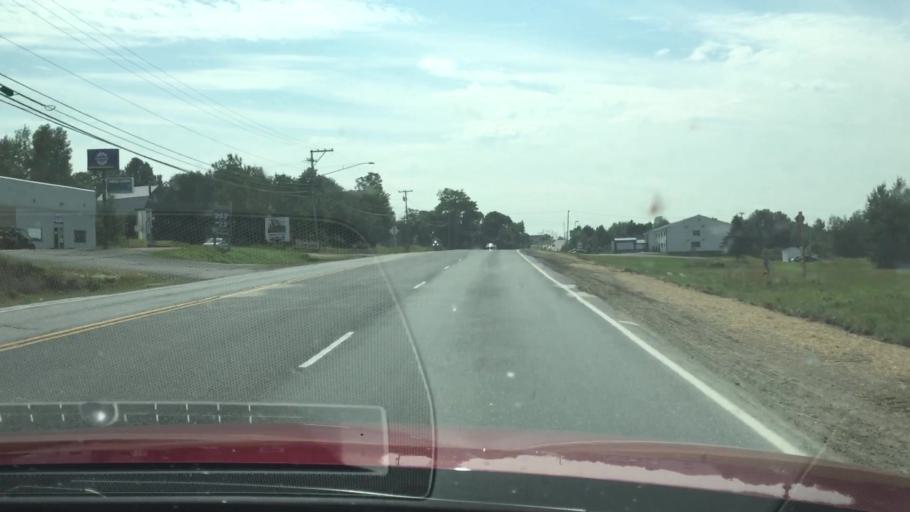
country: US
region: Maine
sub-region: Aroostook County
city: Presque Isle
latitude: 46.6668
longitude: -68.0114
